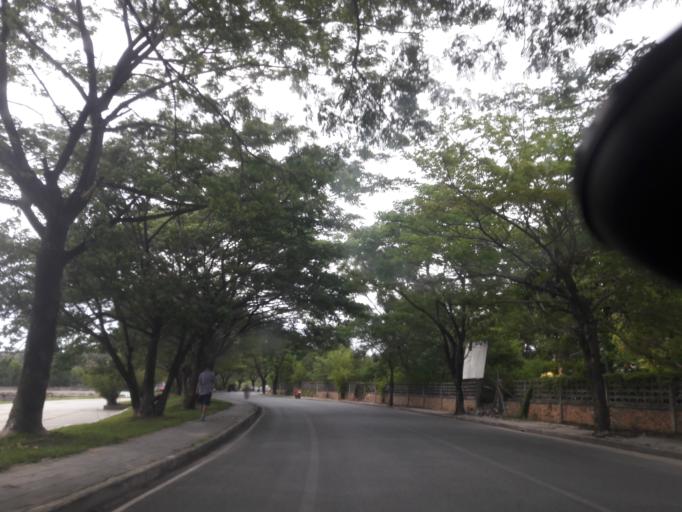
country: TH
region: Surat Thani
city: Ko Samui
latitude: 9.5301
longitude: 100.0600
